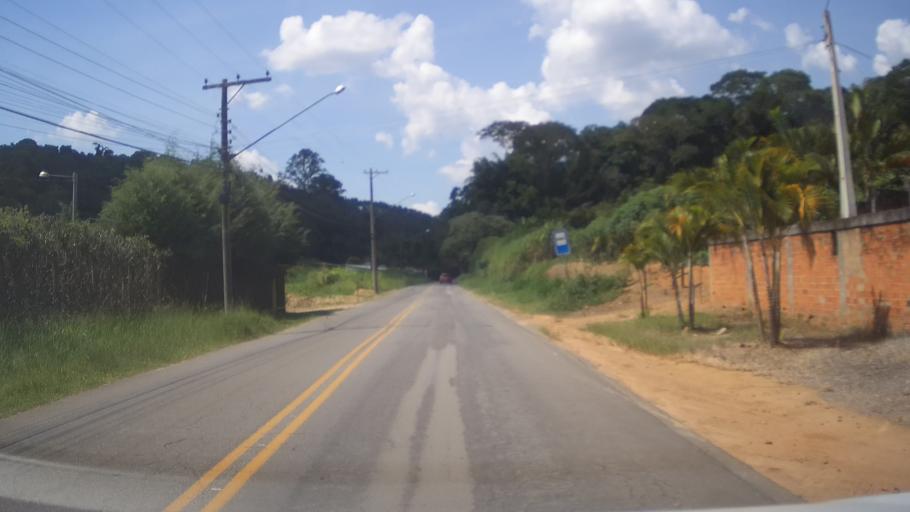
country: BR
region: Sao Paulo
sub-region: Jundiai
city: Jundiai
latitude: -23.1411
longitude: -46.8310
